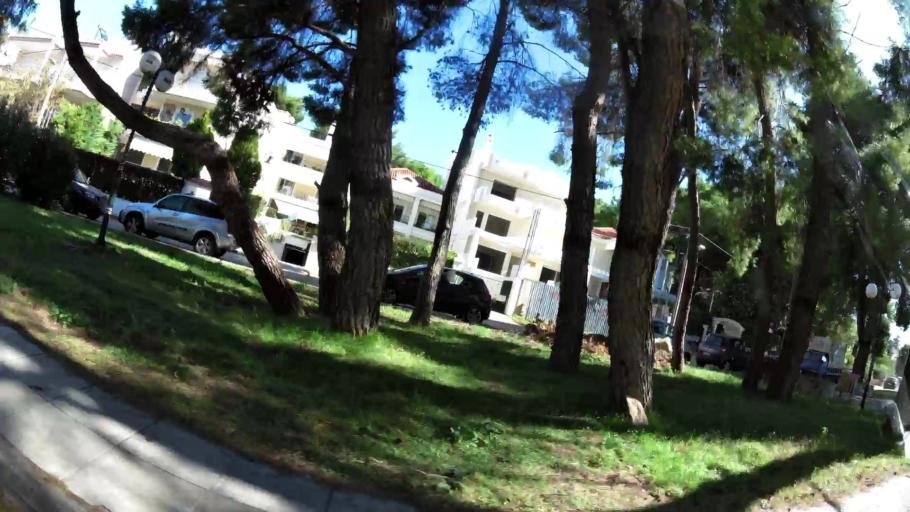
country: GR
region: Attica
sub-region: Nomarchia Anatolikis Attikis
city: Drosia
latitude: 38.1177
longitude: 23.8570
